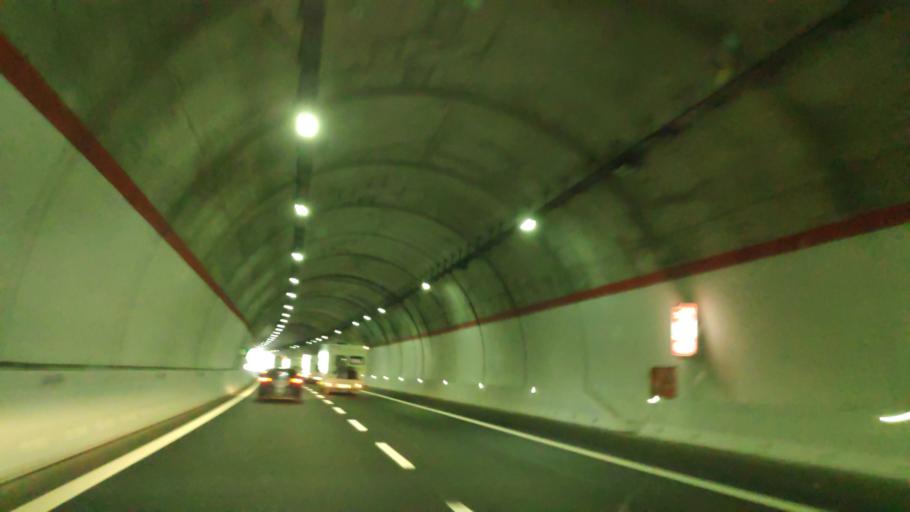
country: IT
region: Campania
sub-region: Provincia di Salerno
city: Casalbuono
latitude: 40.2251
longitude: 15.6717
